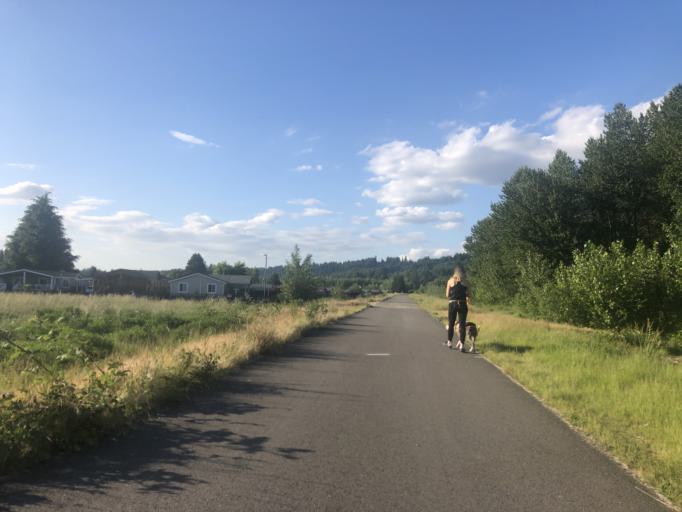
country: US
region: Washington
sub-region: King County
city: Lea Hill
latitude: 47.3374
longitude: -122.2106
